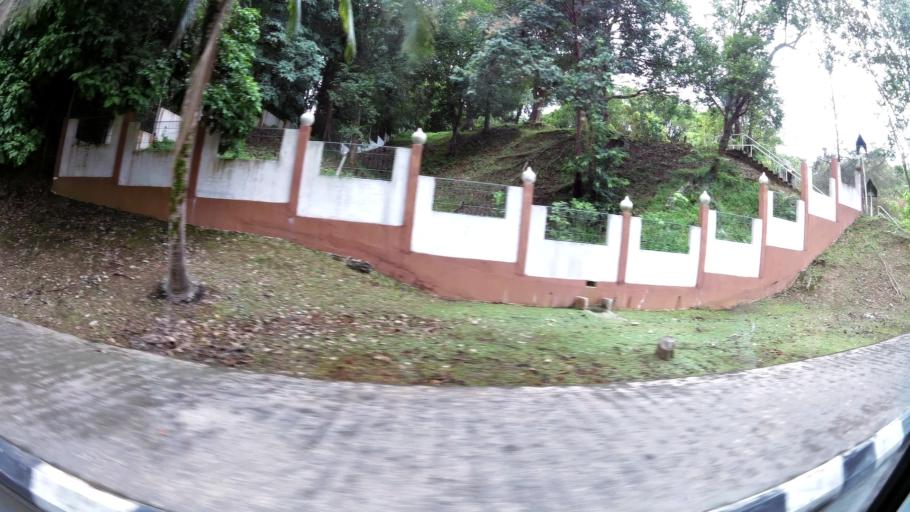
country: BN
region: Brunei and Muara
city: Bandar Seri Begawan
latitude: 4.8845
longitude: 114.9312
